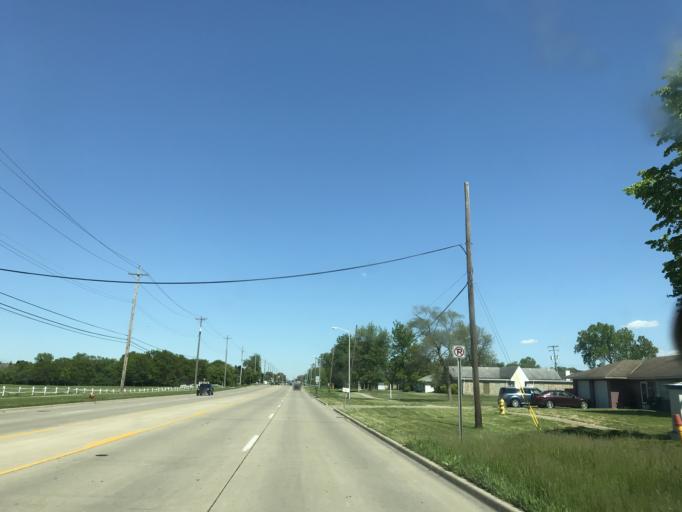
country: US
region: Michigan
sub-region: Wayne County
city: Southgate
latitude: 42.1844
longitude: -83.2183
